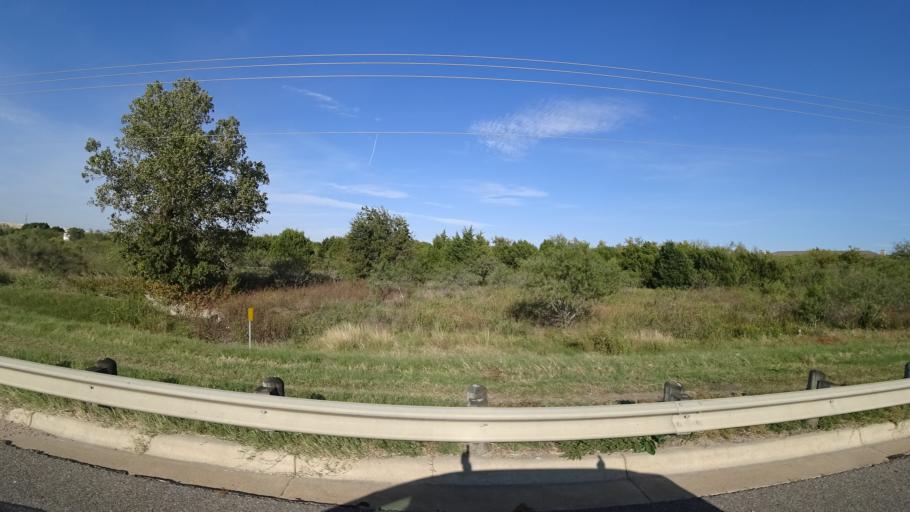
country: US
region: Texas
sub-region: Travis County
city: Wells Branch
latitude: 30.4018
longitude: -97.6563
